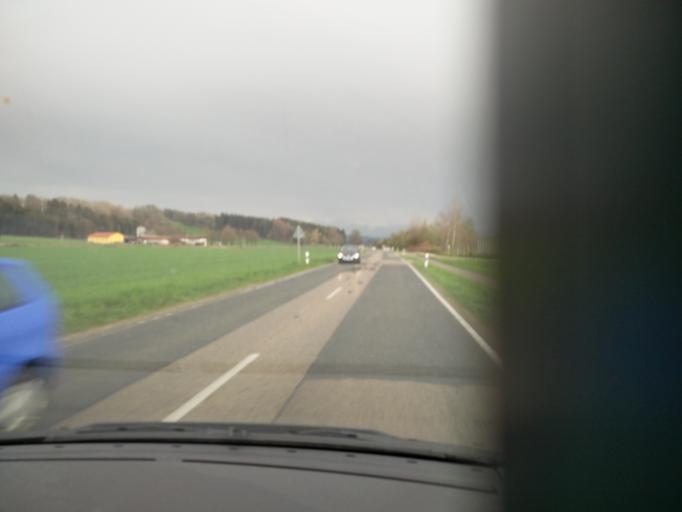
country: DE
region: Bavaria
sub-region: Upper Bavaria
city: Halfing
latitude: 47.9457
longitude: 12.2785
